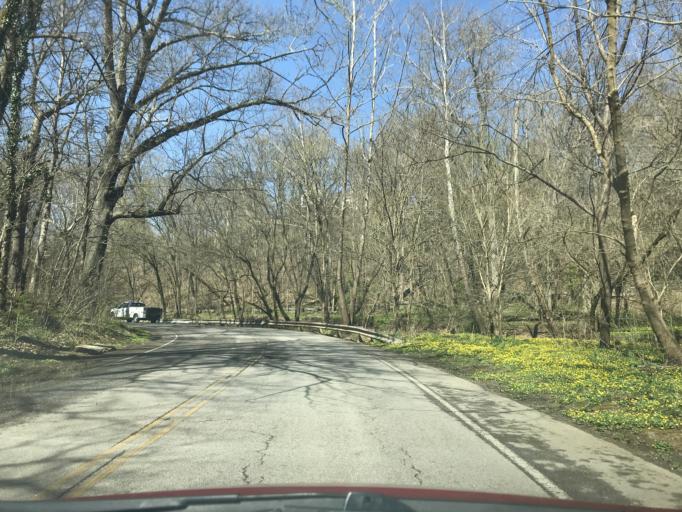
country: US
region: Kentucky
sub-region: Jefferson County
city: Saint Matthews
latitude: 38.2376
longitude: -85.6882
